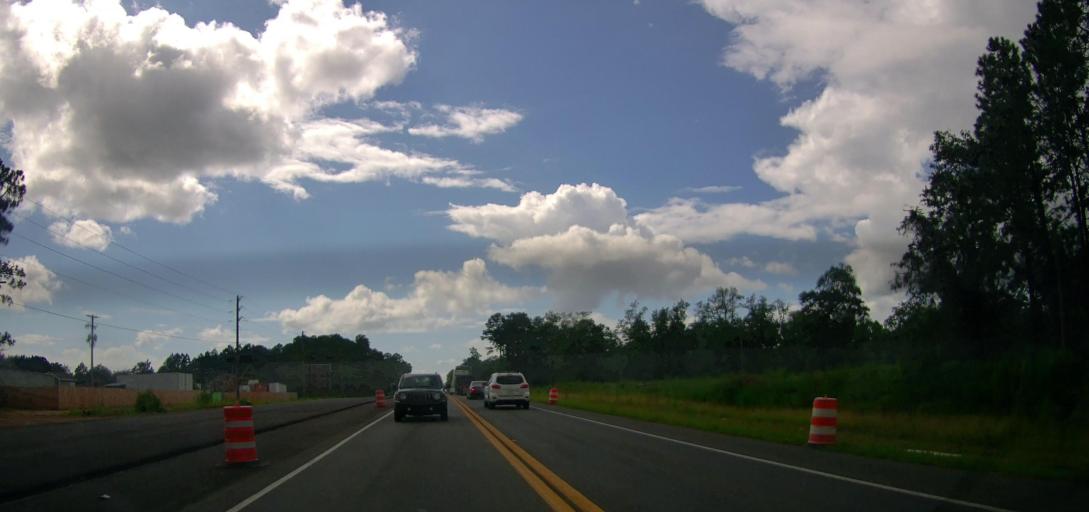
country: US
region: Georgia
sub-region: Coffee County
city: Douglas
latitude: 31.5234
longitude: -82.8975
